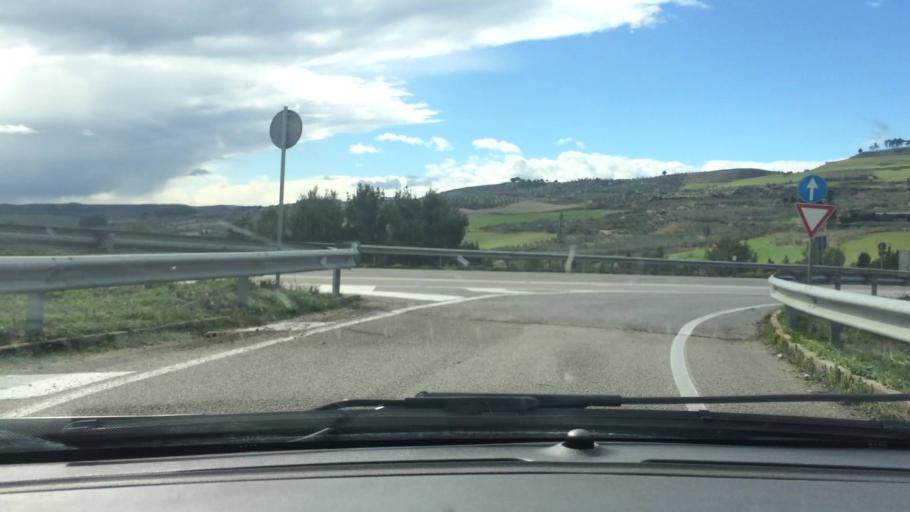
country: IT
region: Apulia
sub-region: Provincia di Bari
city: Gravina in Puglia
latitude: 40.8054
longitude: 16.4209
